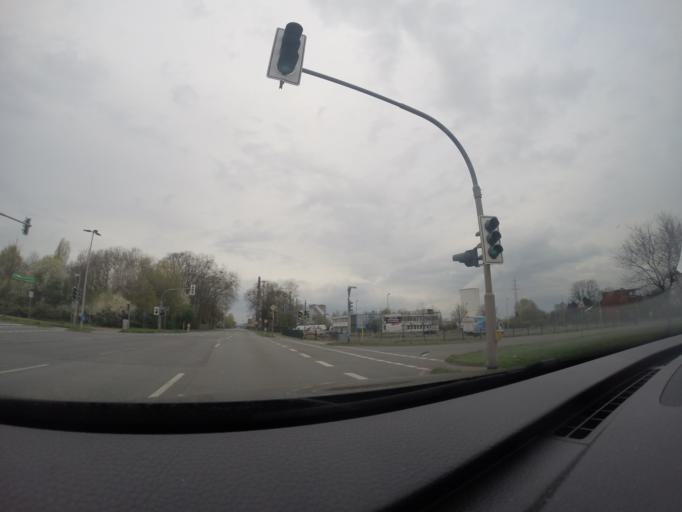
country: DE
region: North Rhine-Westphalia
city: Rheinberg
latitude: 51.5591
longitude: 6.5854
